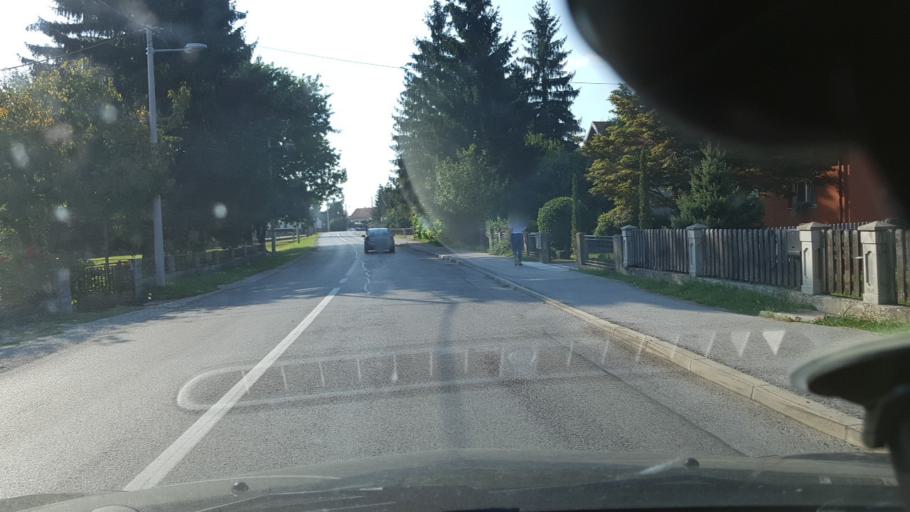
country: HR
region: Zagrebacka
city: Brdovec
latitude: 45.8684
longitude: 15.7571
